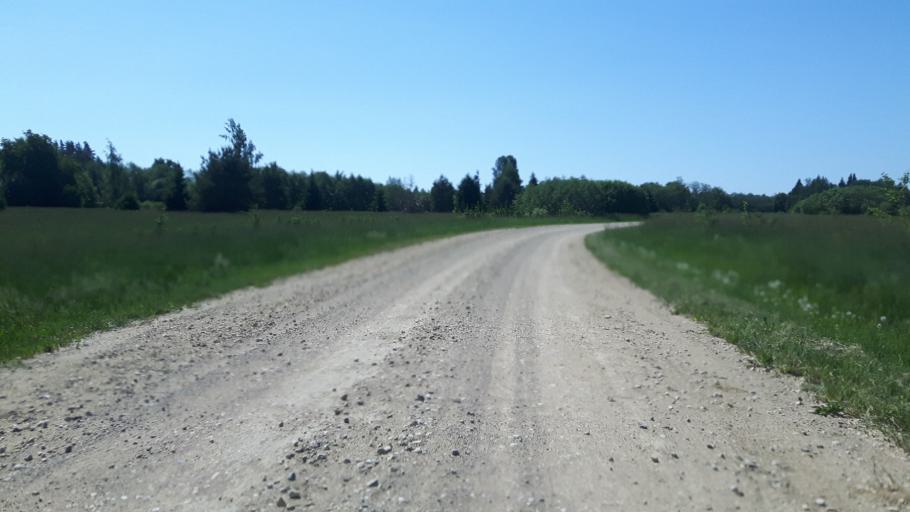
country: EE
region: Paernumaa
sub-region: Vaendra vald (alev)
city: Vandra
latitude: 58.5541
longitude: 24.9506
